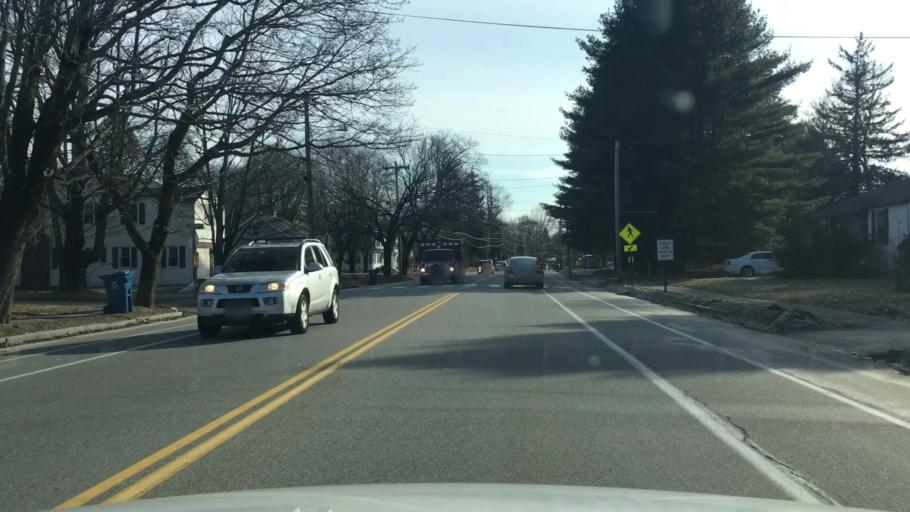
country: US
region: Maine
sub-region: Cumberland County
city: South Portland Gardens
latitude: 43.6958
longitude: -70.3050
